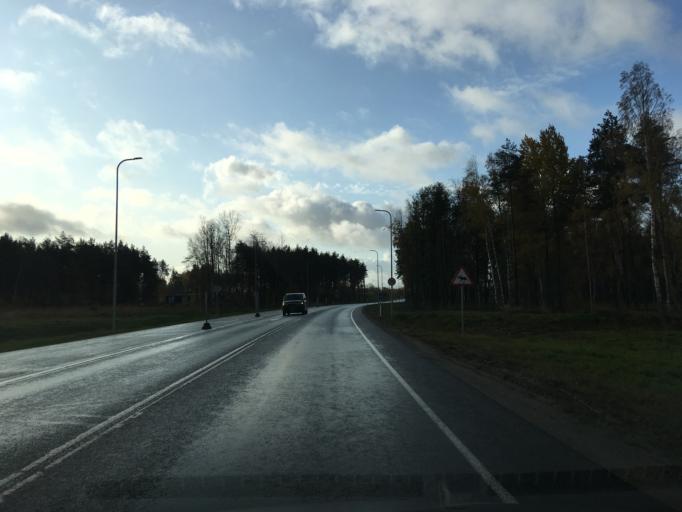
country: EE
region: Harju
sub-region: Saue vald
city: Laagri
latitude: 59.3577
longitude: 24.6005
